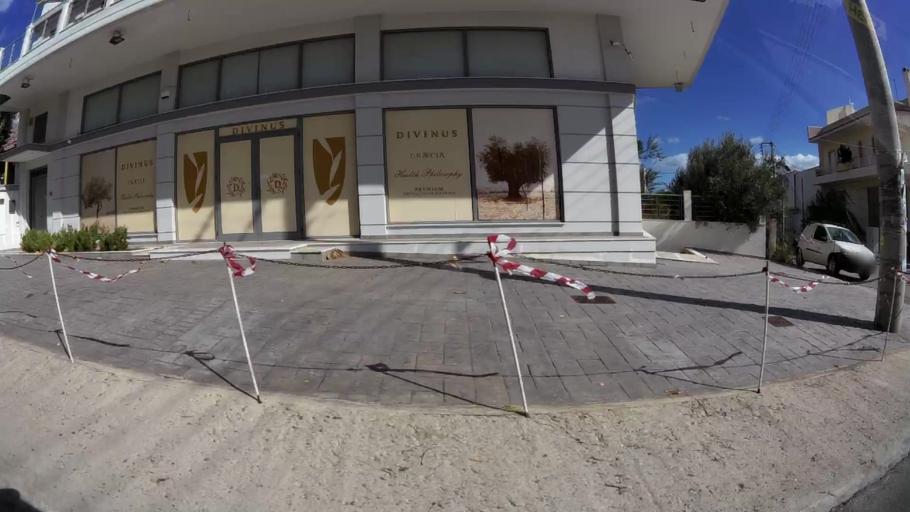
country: GR
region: Attica
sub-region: Nomarchia Anatolikis Attikis
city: Acharnes
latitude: 38.1061
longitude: 23.7364
